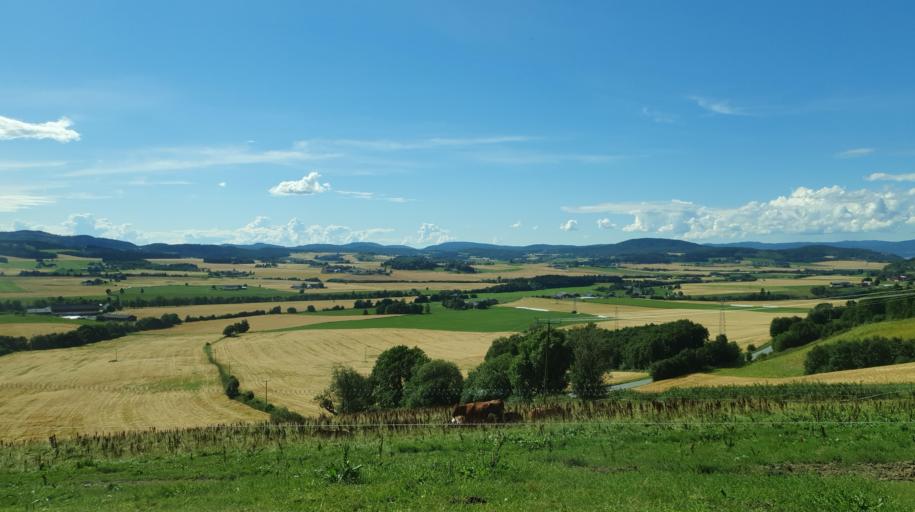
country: NO
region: Nord-Trondelag
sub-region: Levanger
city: Skogn
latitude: 63.6860
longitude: 11.2382
